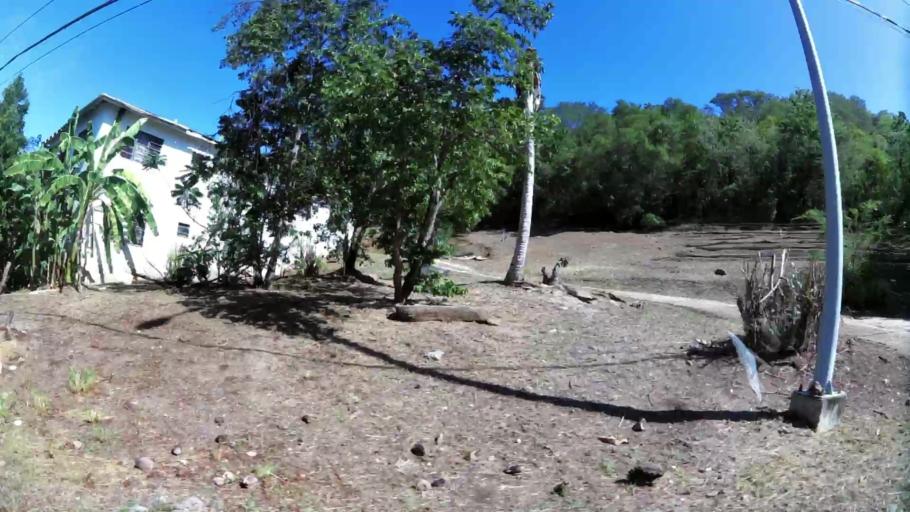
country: AG
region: Saint Paul
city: Falmouth
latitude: 17.0138
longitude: -61.7613
